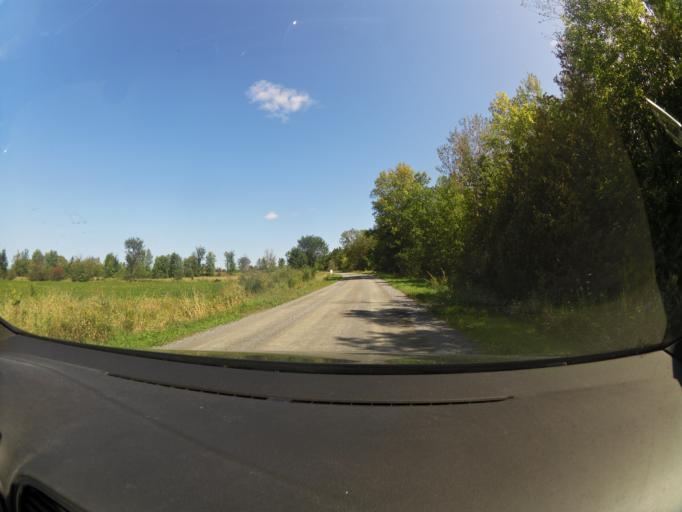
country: CA
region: Ontario
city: Arnprior
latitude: 45.3028
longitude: -76.2699
